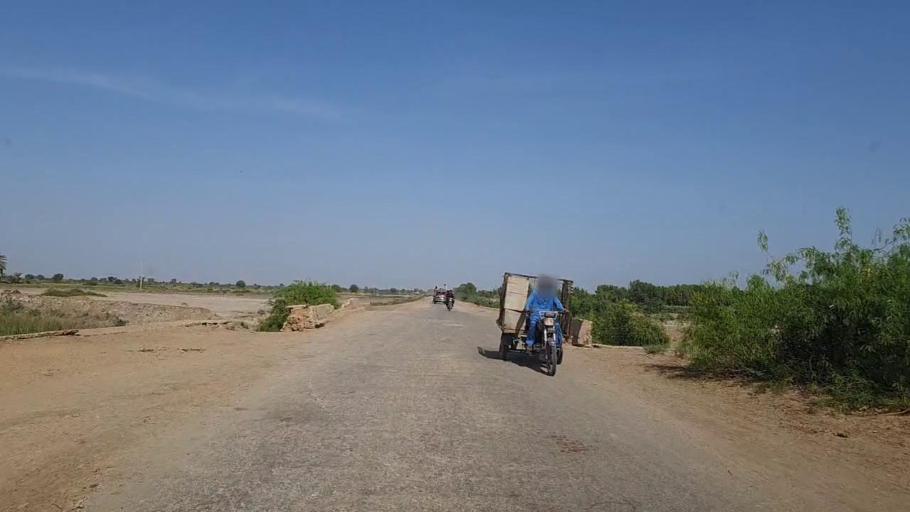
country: PK
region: Sindh
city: Kotri
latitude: 25.1601
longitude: 68.2462
